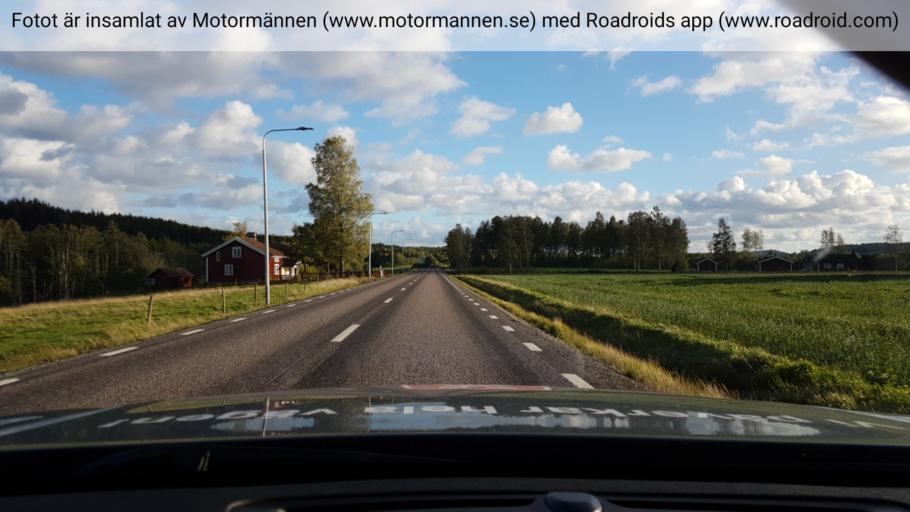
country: SE
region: Vaermland
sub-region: Karlstads Kommun
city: Molkom
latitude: 59.7121
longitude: 13.6786
